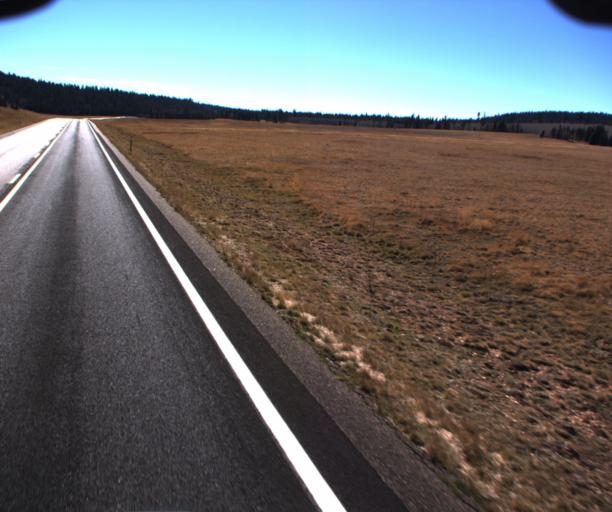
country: US
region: Arizona
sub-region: Coconino County
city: Grand Canyon
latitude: 36.4838
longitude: -112.1282
